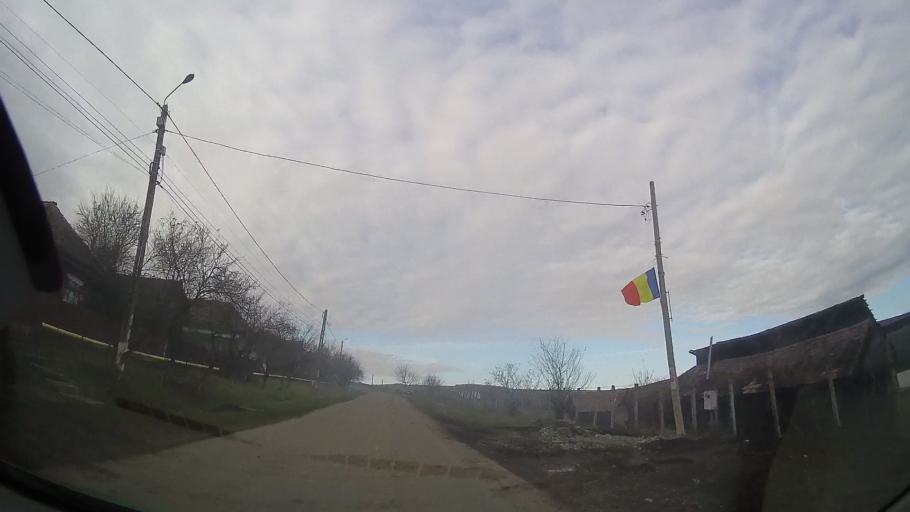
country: RO
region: Cluj
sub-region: Comuna Catina
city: Catina
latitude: 46.8484
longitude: 24.1558
